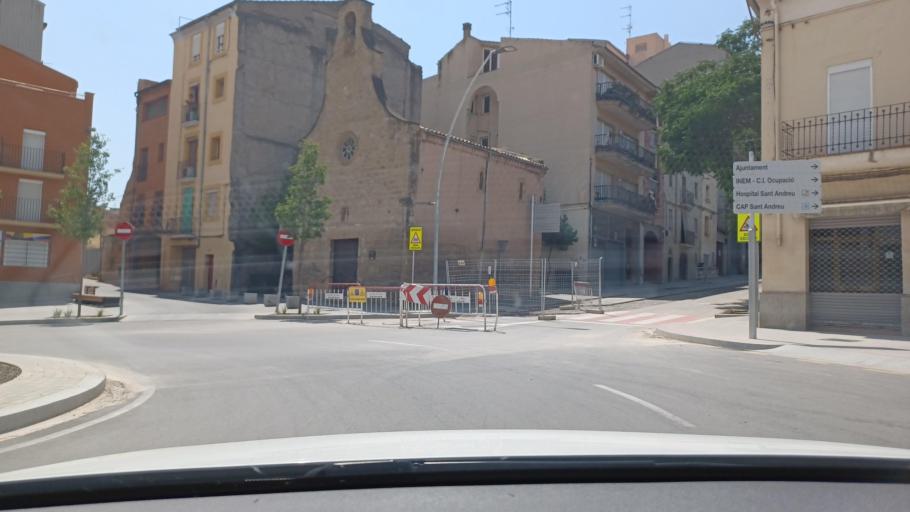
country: ES
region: Catalonia
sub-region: Provincia de Barcelona
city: Manresa
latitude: 41.7273
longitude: 1.8320
